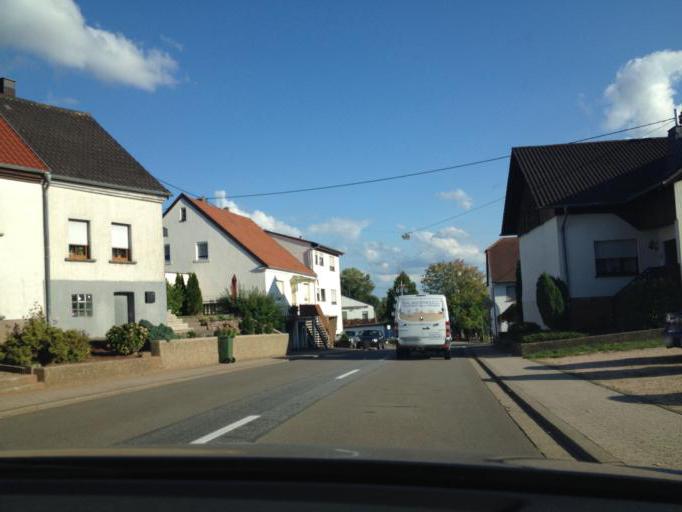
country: DE
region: Saarland
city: Eppelborn
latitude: 49.4746
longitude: 6.9613
